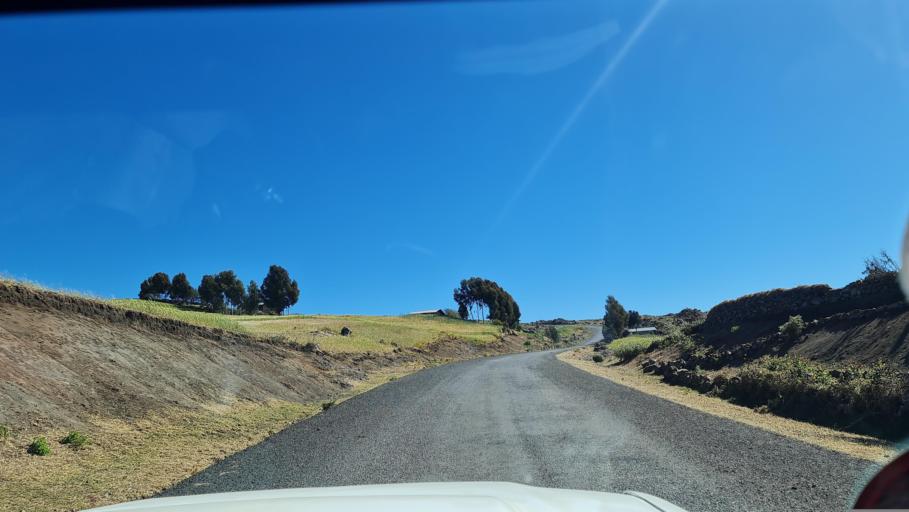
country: ET
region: Amhara
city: Debark'
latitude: 13.1340
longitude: 38.1721
